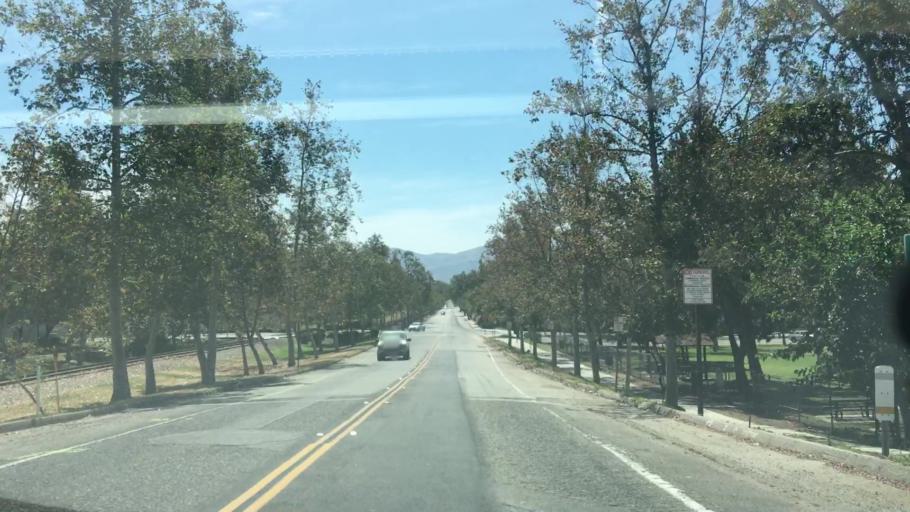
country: US
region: California
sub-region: Ventura County
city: Fillmore
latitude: 34.4051
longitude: -118.9301
